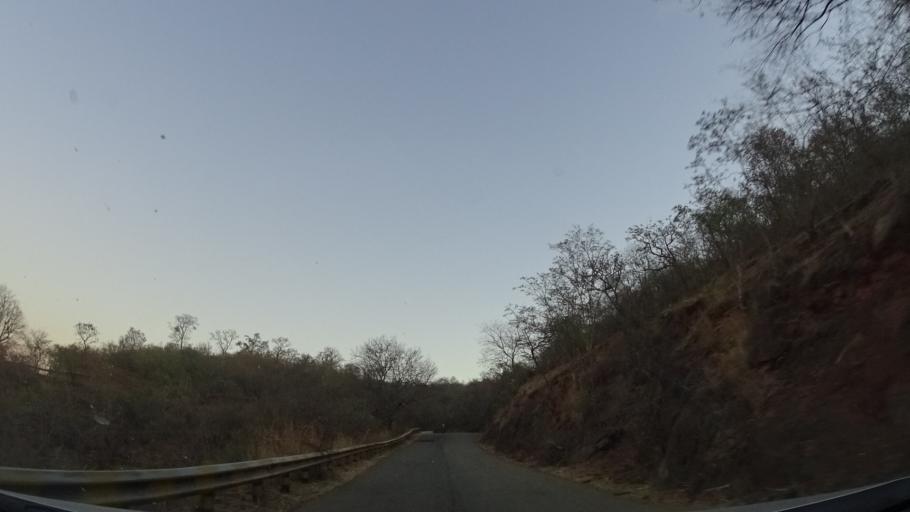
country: IN
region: Karnataka
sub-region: Chikmagalur
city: Birur
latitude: 13.5498
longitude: 75.8223
